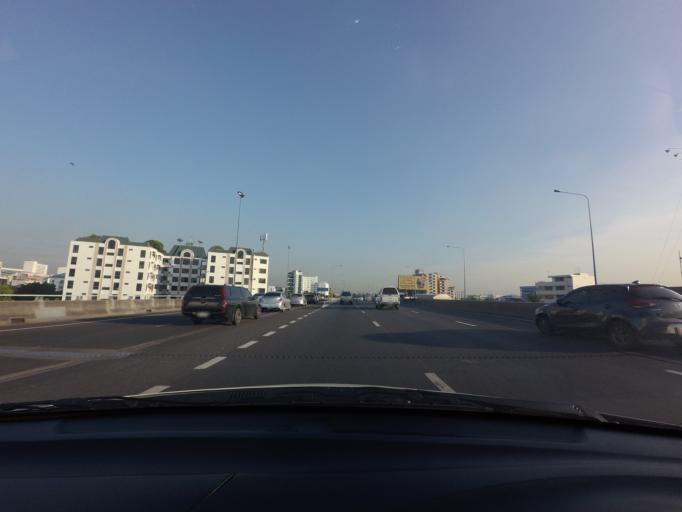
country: TH
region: Nonthaburi
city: Mueang Nonthaburi
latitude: 13.8621
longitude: 100.5332
